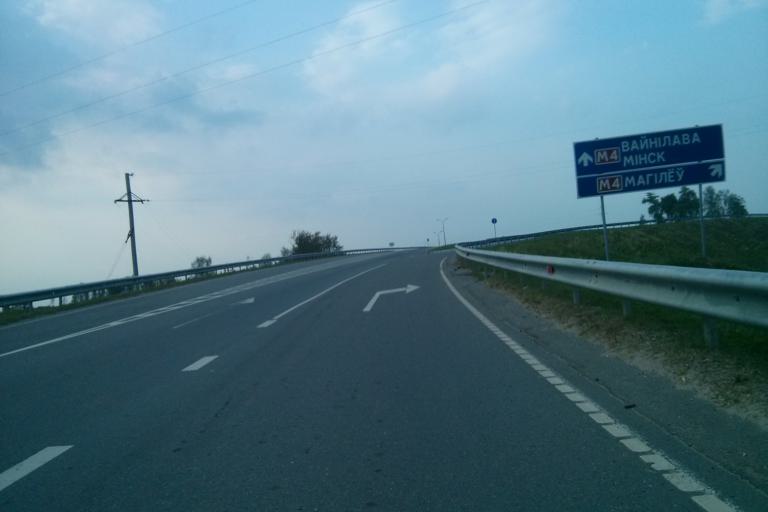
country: BY
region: Minsk
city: Chervyen'
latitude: 53.7213
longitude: 28.3957
